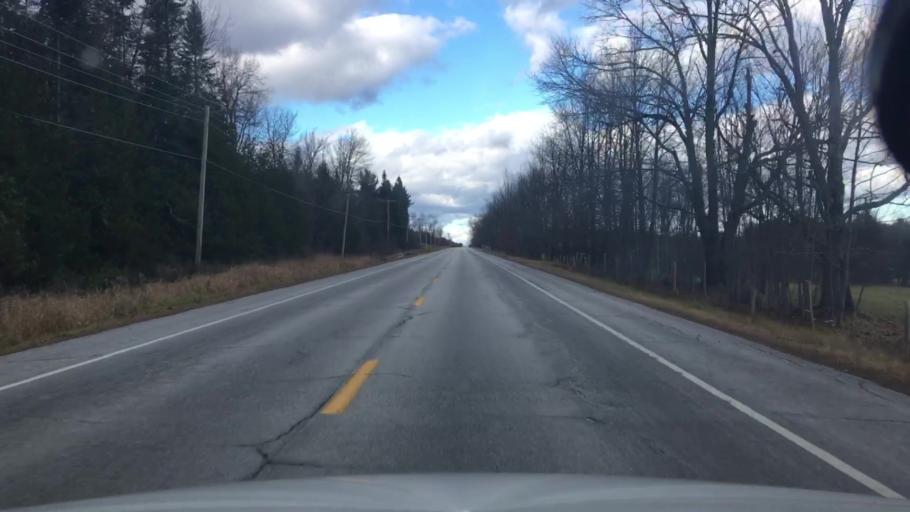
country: US
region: Maine
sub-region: Somerset County
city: Pittsfield
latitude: 44.8144
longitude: -69.4076
